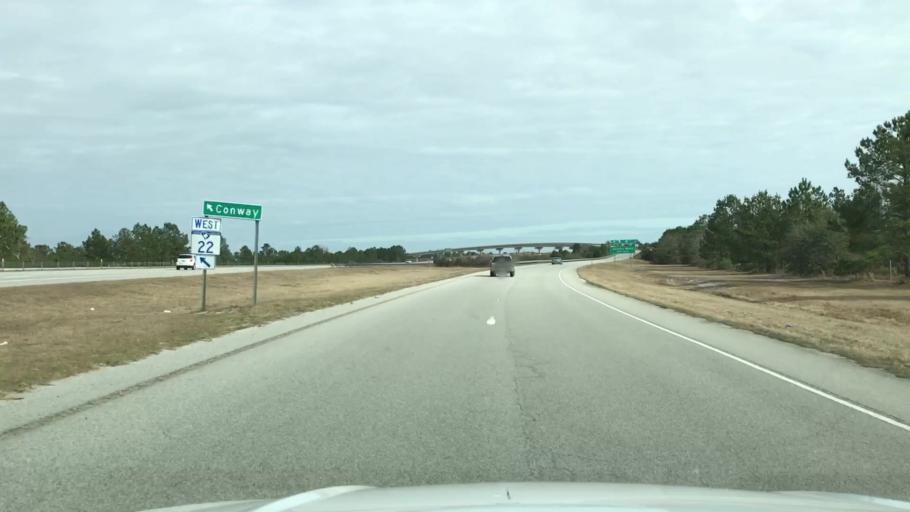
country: US
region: South Carolina
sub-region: Horry County
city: North Myrtle Beach
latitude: 33.8074
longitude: -78.7885
